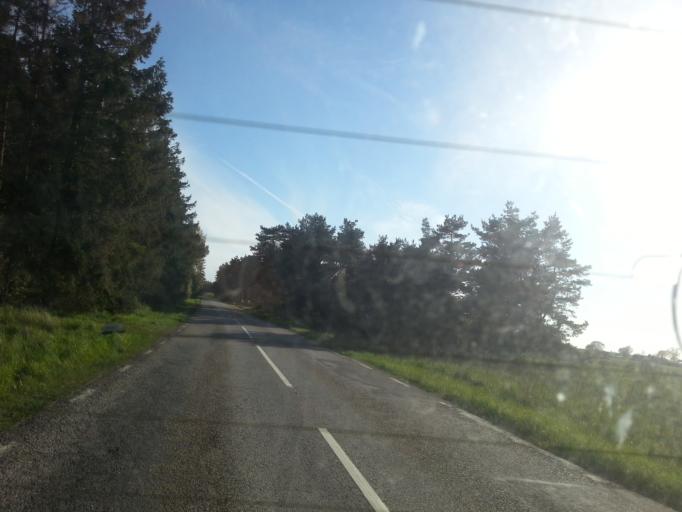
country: SE
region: Skane
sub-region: Simrishamns Kommun
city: Simrishamn
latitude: 55.4099
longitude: 14.1928
